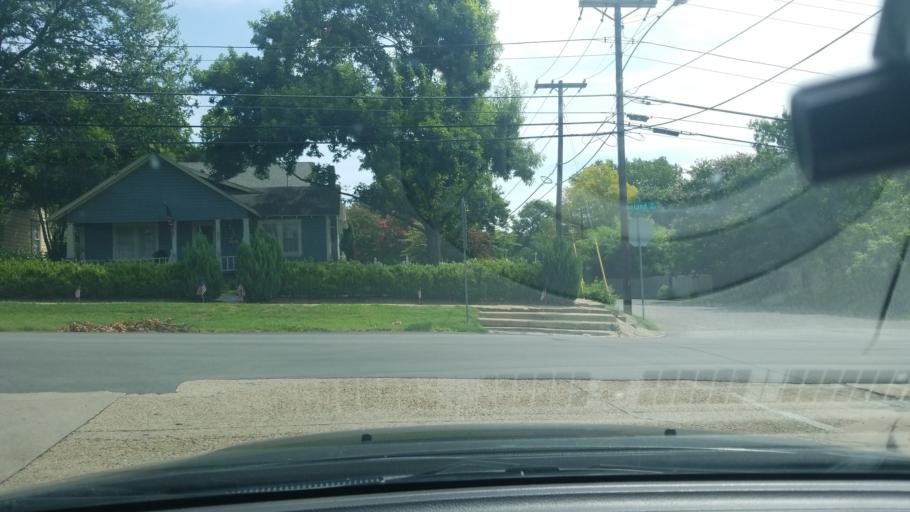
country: US
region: Texas
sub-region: Dallas County
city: Highland Park
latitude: 32.8168
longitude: -96.7073
